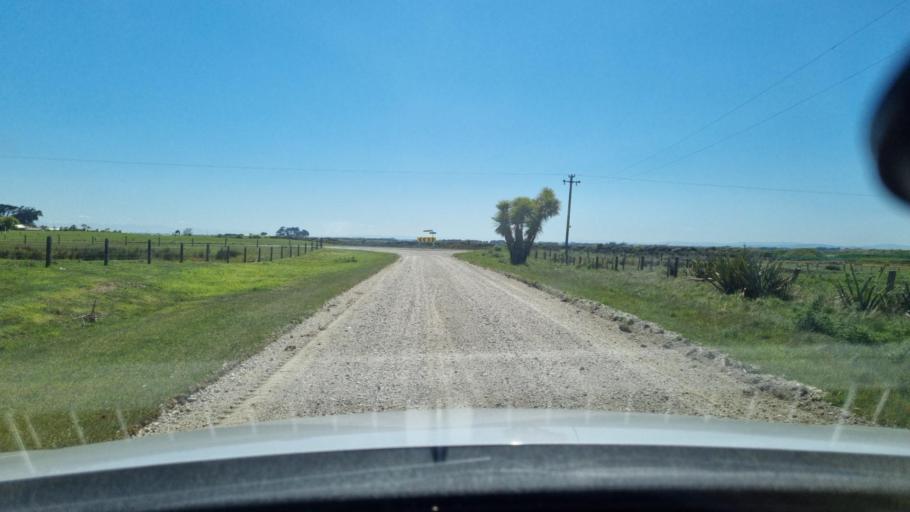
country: NZ
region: Southland
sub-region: Invercargill City
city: Invercargill
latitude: -46.4101
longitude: 168.2634
